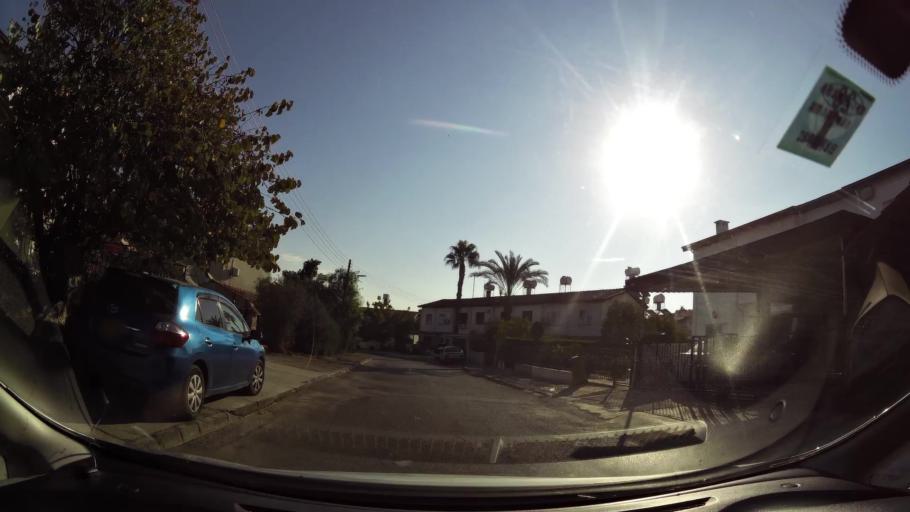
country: CY
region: Lefkosia
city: Nicosia
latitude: 35.2080
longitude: 33.3509
